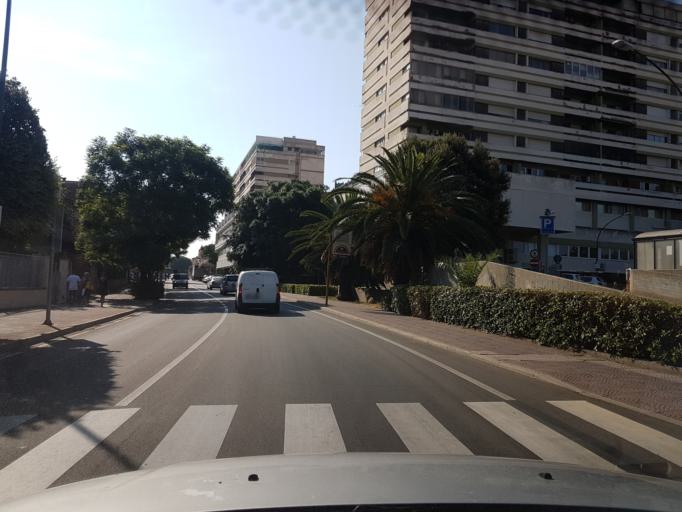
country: IT
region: Sardinia
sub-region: Provincia di Oristano
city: Oristano
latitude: 39.9022
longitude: 8.5889
